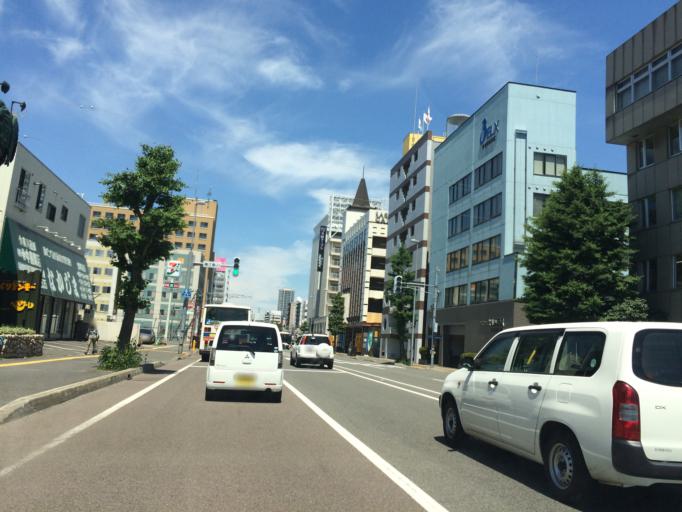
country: JP
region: Hokkaido
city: Sapporo
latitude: 43.0501
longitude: 141.3424
